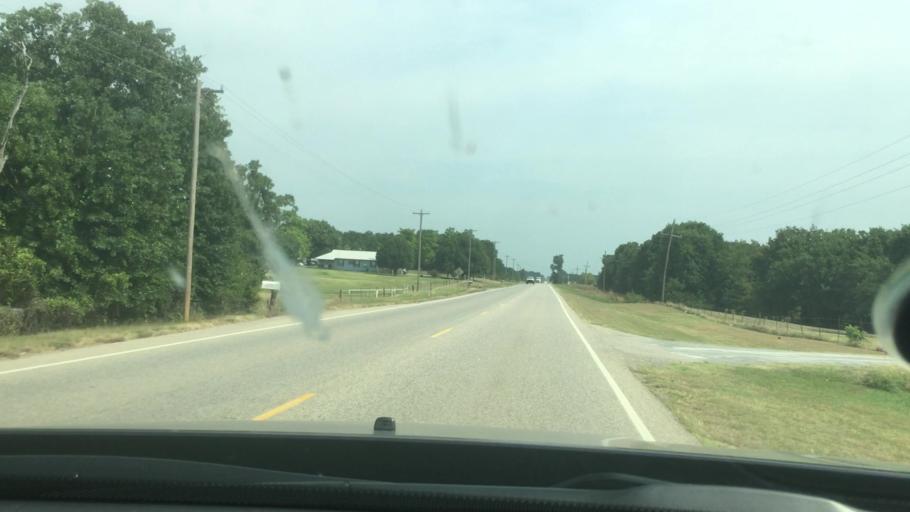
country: US
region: Oklahoma
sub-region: Bryan County
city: Durant
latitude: 34.2049
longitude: -96.4250
